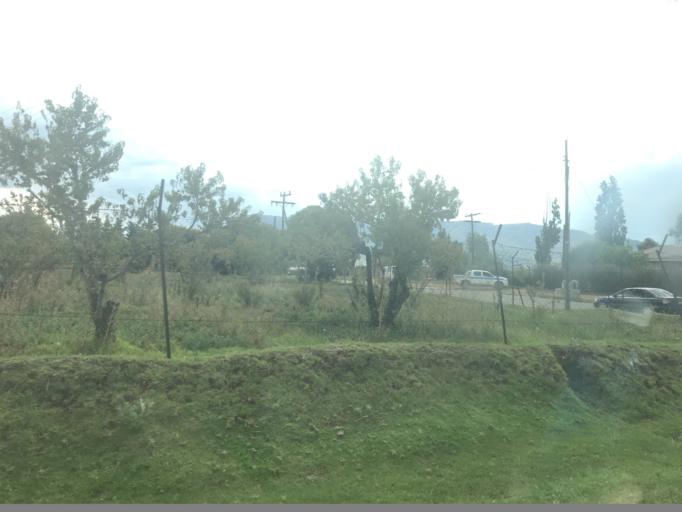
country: LS
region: Maseru
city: Nako
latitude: -29.6236
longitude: 27.5032
